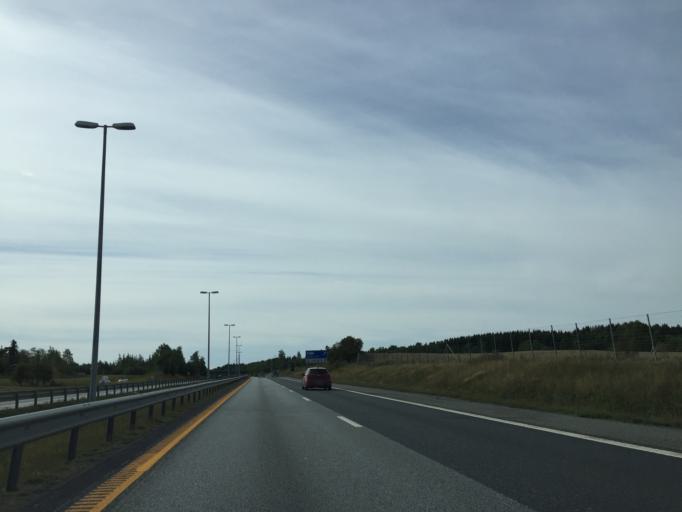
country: NO
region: Akershus
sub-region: Vestby
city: Vestby
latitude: 59.6302
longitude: 10.7367
